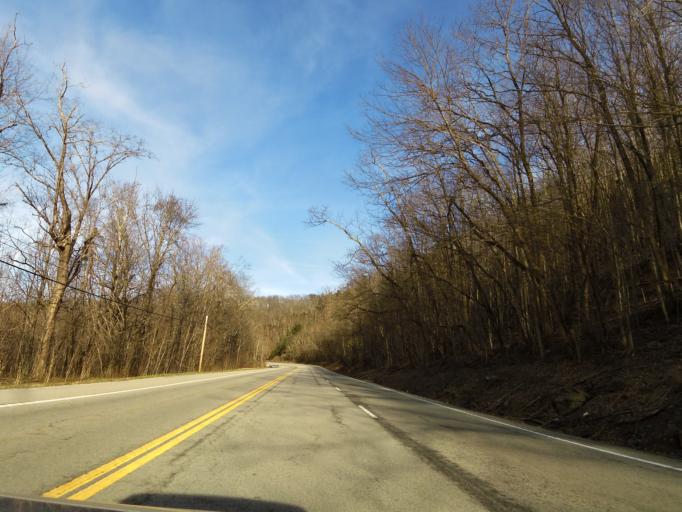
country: US
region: Tennessee
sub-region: White County
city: Sparta
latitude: 35.9236
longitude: -85.3878
